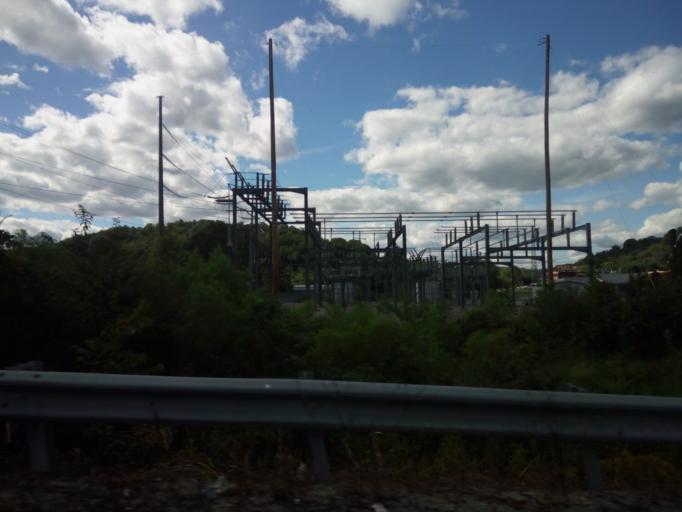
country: US
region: Tennessee
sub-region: Campbell County
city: Jellico
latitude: 36.5787
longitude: -84.1128
